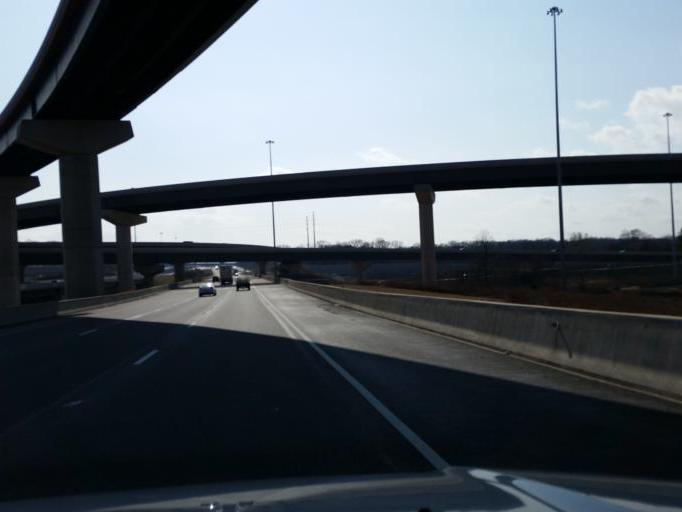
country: US
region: Maryland
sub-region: Baltimore County
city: Rossville
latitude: 39.3528
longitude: -76.4949
